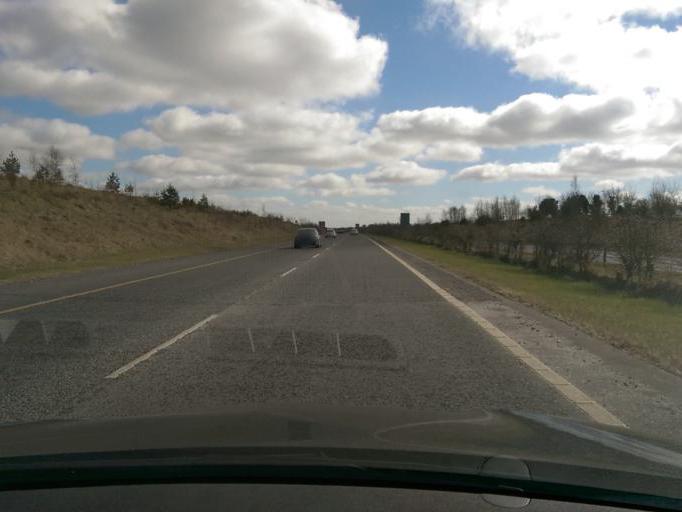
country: IE
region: Leinster
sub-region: An Iarmhi
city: Kinnegad
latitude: 53.4471
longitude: -7.0805
